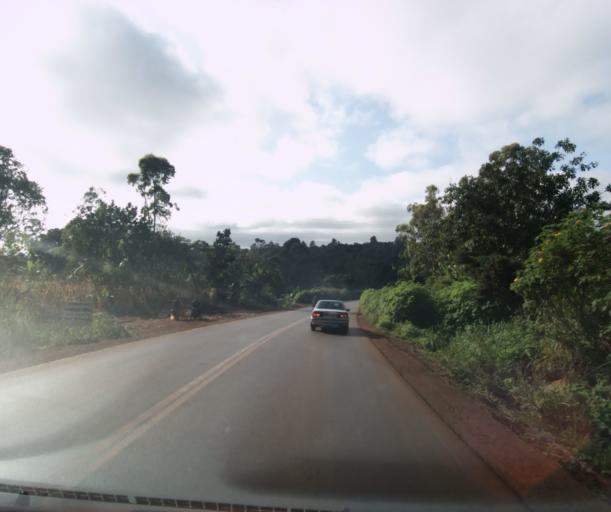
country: CM
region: West
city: Mbouda
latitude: 5.6052
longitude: 10.2931
